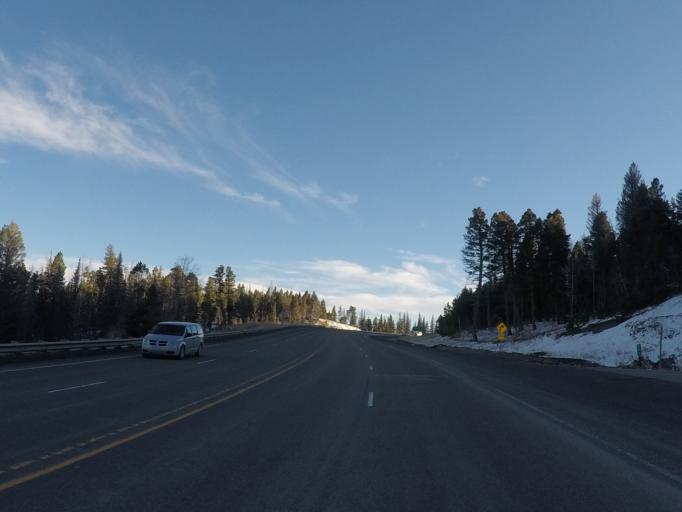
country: US
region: Montana
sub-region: Lewis and Clark County
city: Helena West Side
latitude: 46.5659
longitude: -112.3063
